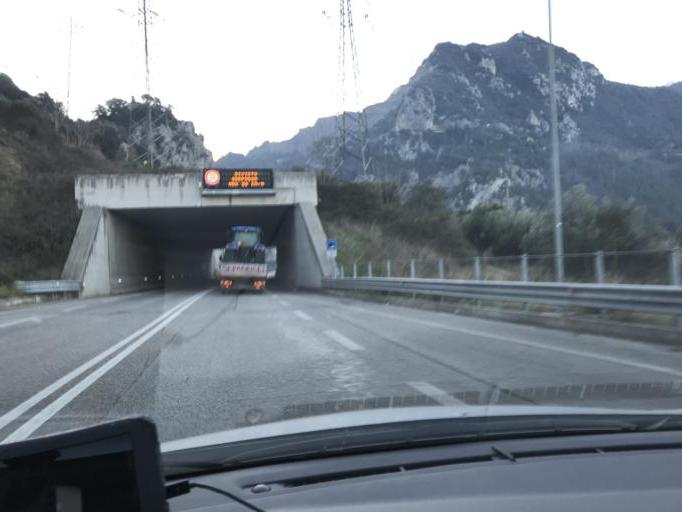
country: IT
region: Umbria
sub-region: Provincia di Terni
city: Terni
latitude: 42.5551
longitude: 12.6971
